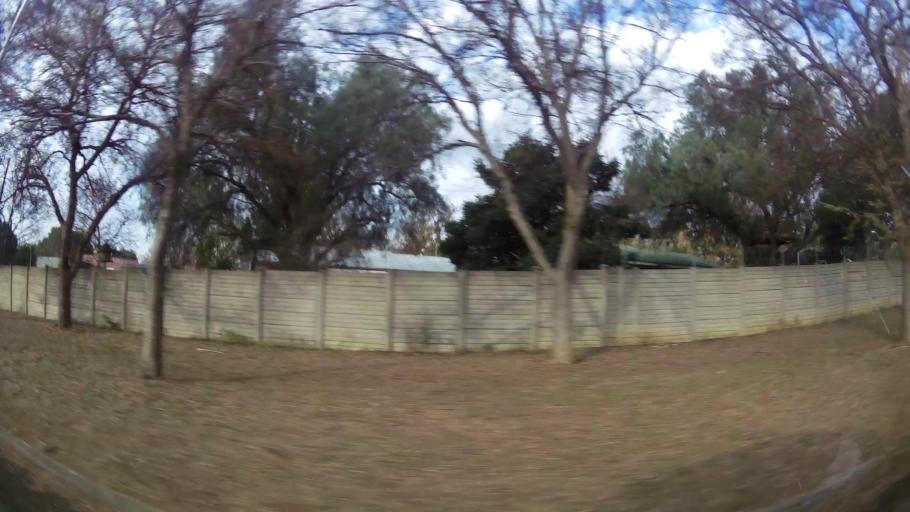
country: ZA
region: Orange Free State
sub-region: Fezile Dabi District Municipality
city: Sasolburg
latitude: -26.8115
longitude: 27.8094
